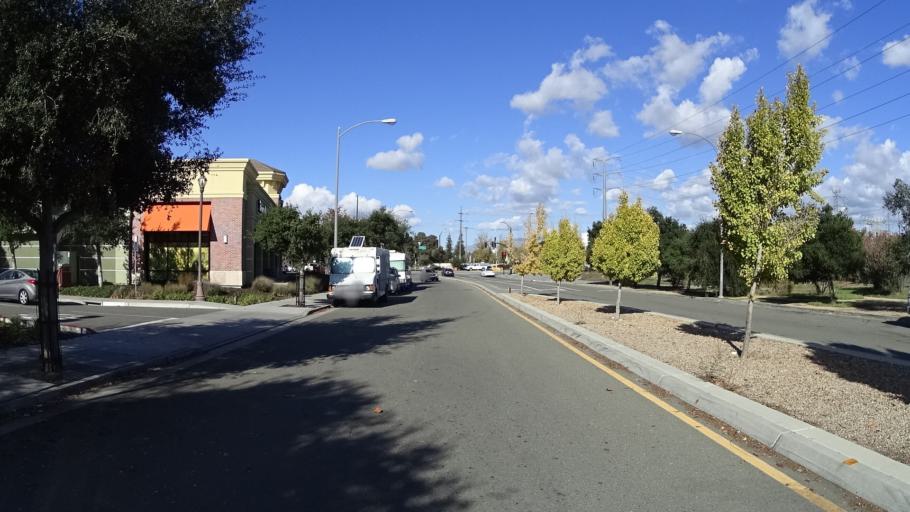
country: US
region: California
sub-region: Santa Clara County
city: San Jose
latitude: 37.3399
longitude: -121.9035
